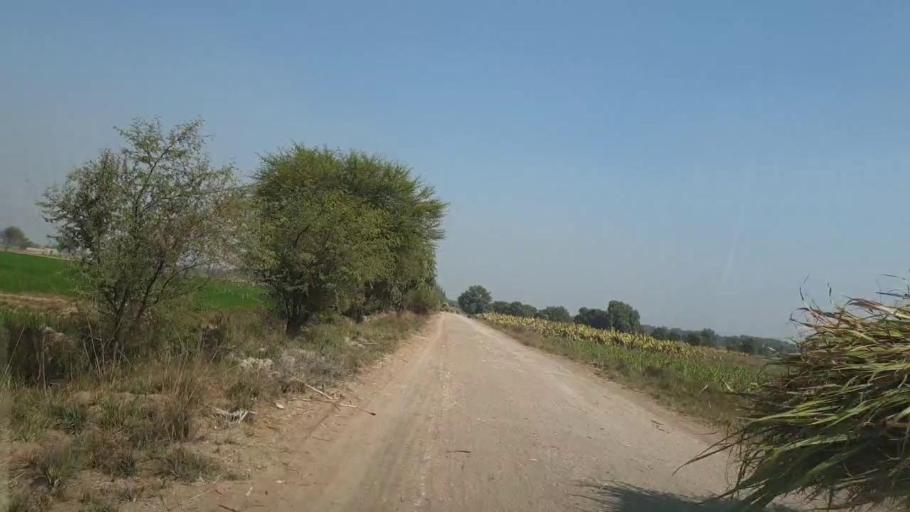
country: PK
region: Sindh
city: Matiari
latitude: 25.5389
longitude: 68.4737
